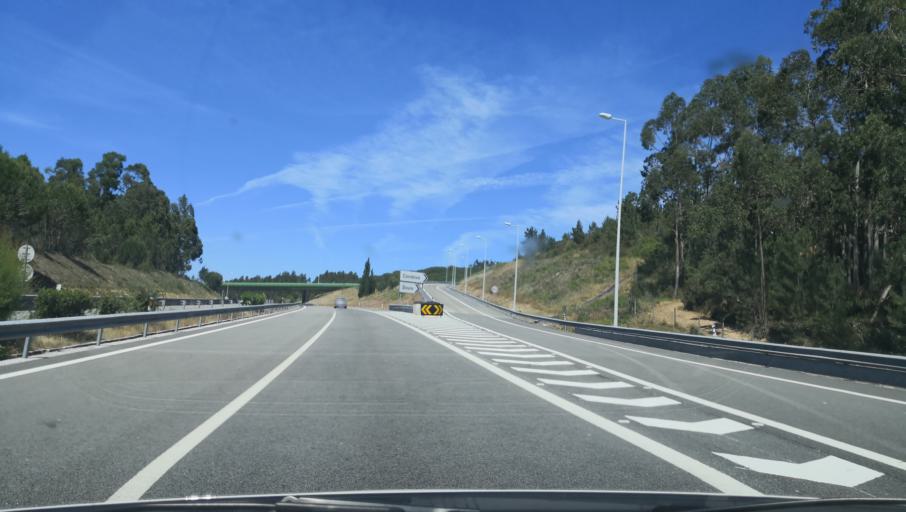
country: PT
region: Coimbra
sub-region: Montemor-O-Velho
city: Montemor-o-Velho
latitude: 40.2002
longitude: -8.6774
